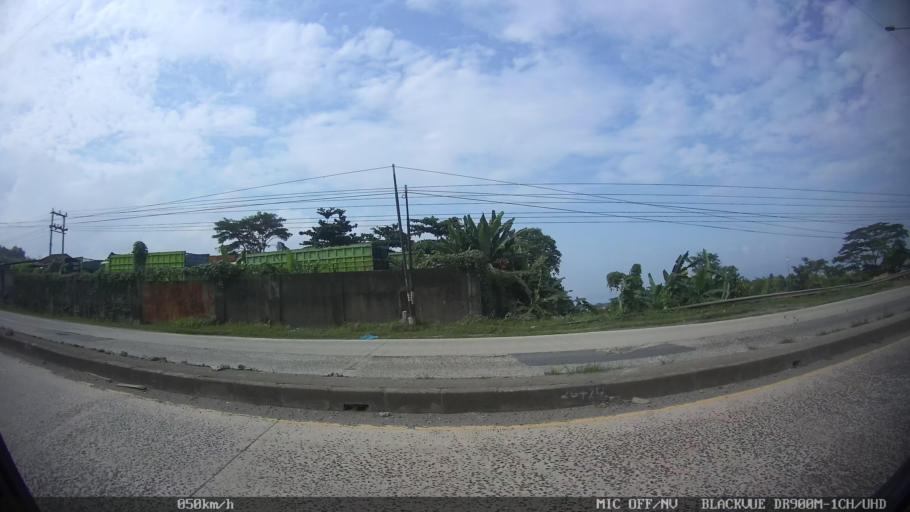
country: ID
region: Lampung
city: Panjang
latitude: -5.4378
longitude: 105.3025
